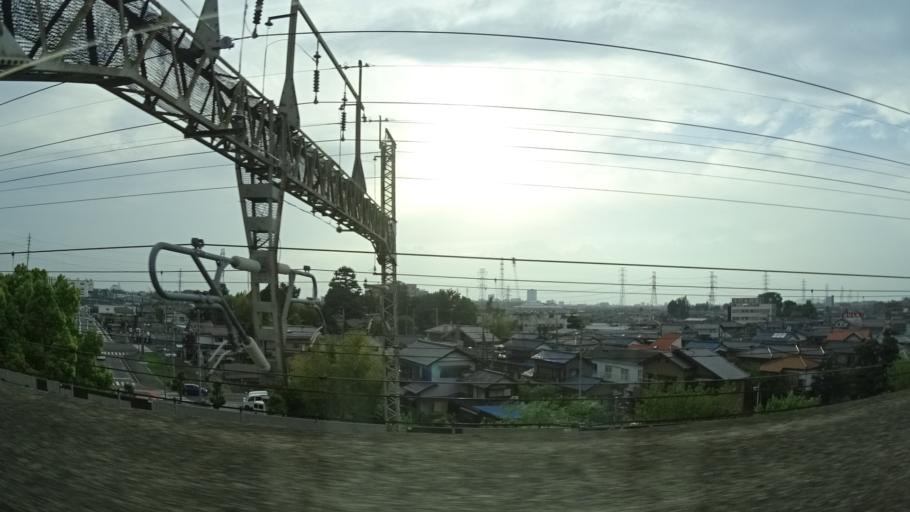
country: JP
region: Saitama
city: Ageoshimo
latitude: 35.9679
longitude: 139.6231
